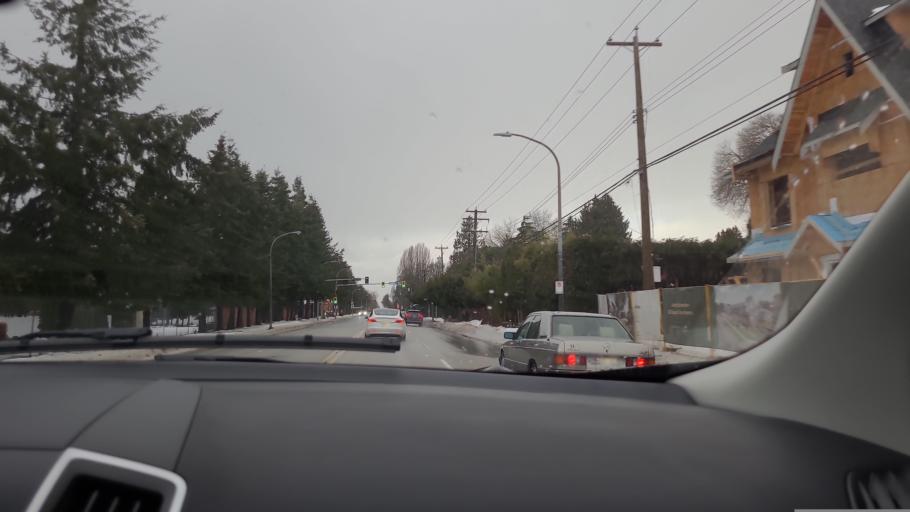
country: CA
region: British Columbia
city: Richmond
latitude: 49.1335
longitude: -123.1201
